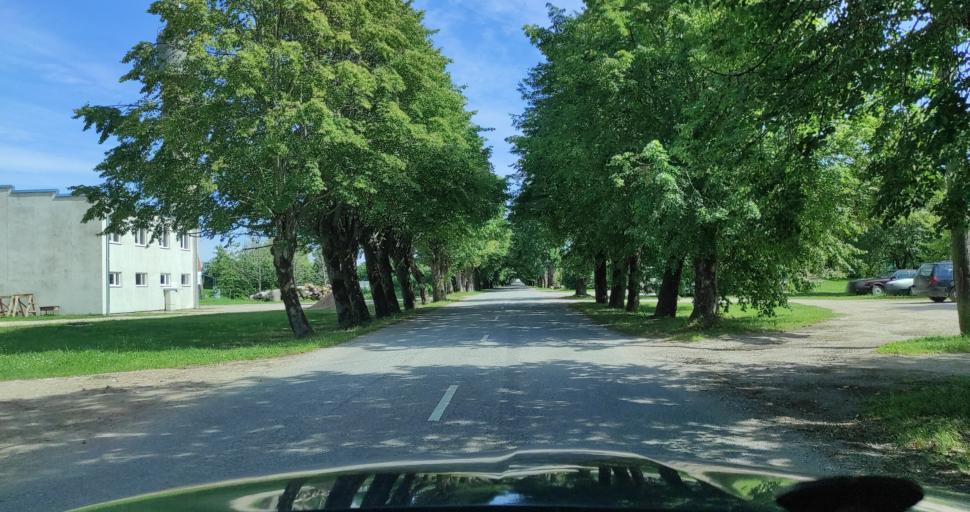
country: LV
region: Durbe
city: Liegi
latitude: 56.7333
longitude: 21.3897
